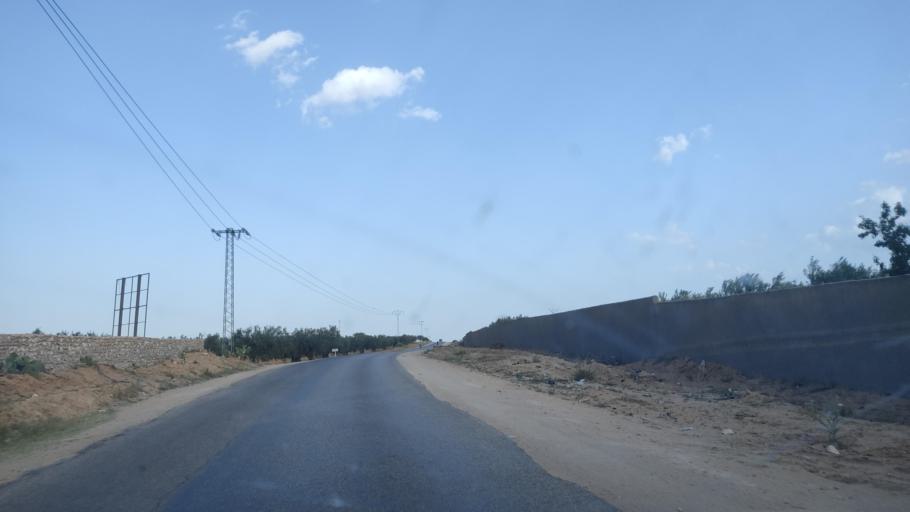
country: TN
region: Safaqis
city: Sfax
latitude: 34.8424
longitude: 10.6215
